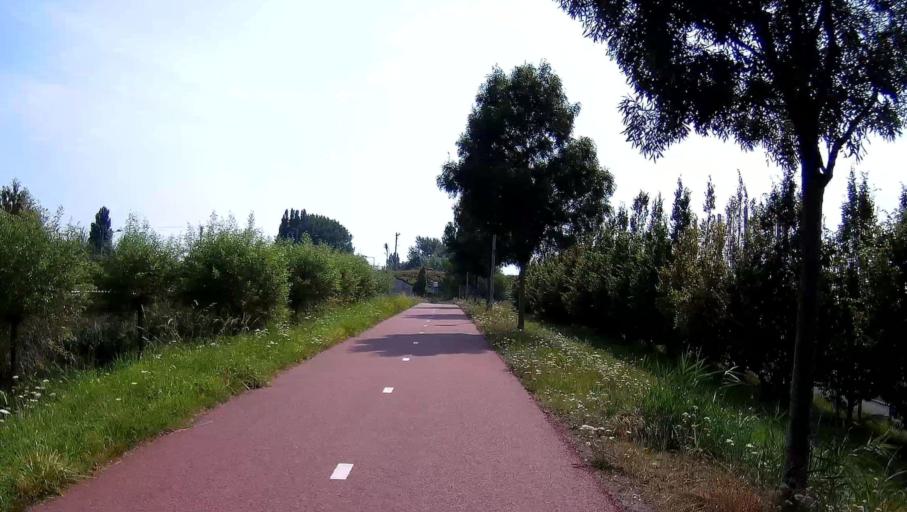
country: NL
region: South Holland
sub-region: Gemeente Den Haag
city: Ypenburg
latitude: 52.0548
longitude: 4.4076
